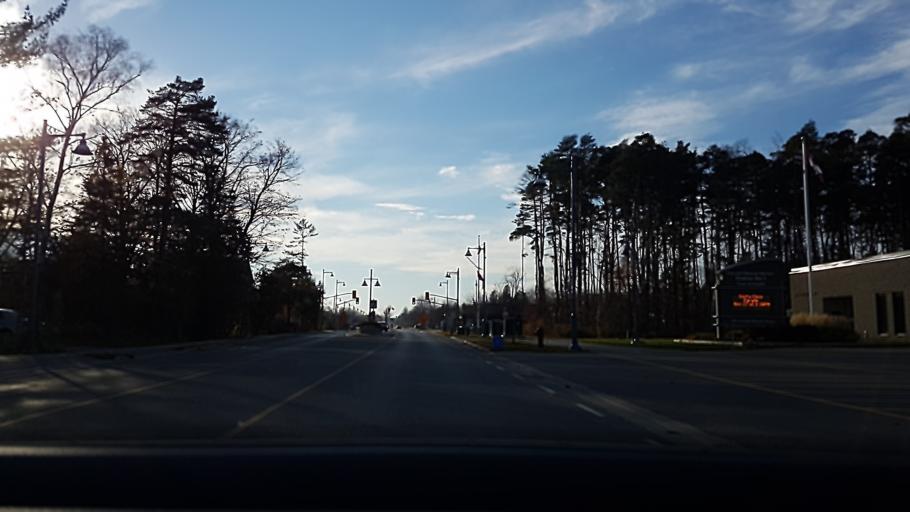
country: CA
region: Ontario
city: Keswick
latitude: 44.3170
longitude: -79.5384
